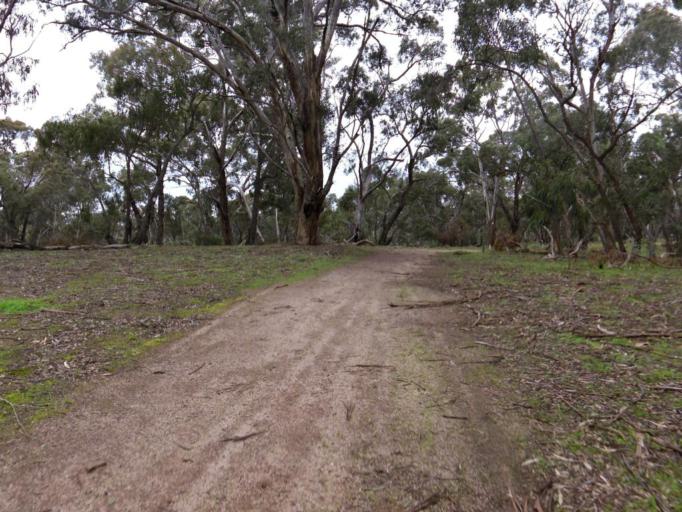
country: AU
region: Victoria
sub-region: Banyule
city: Watsonia North
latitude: -37.6776
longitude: 145.0900
